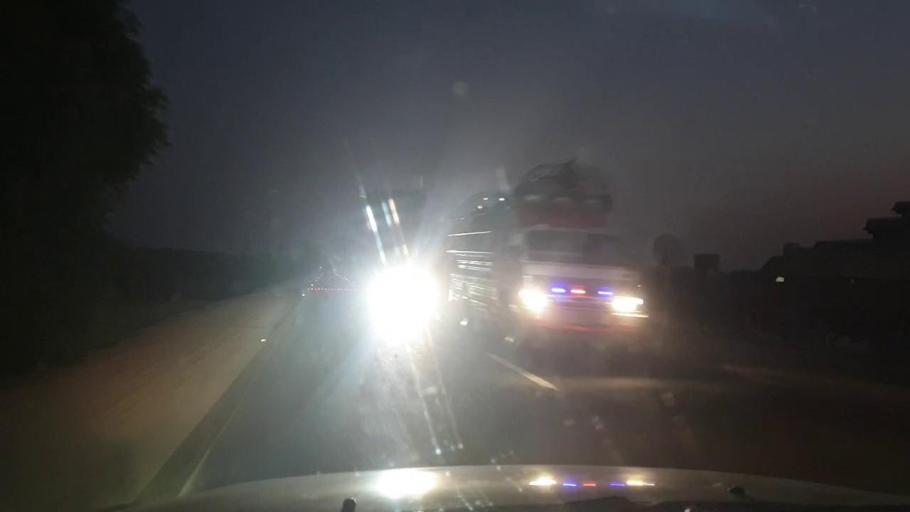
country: PK
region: Sindh
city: Chambar
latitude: 25.3747
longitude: 68.7797
